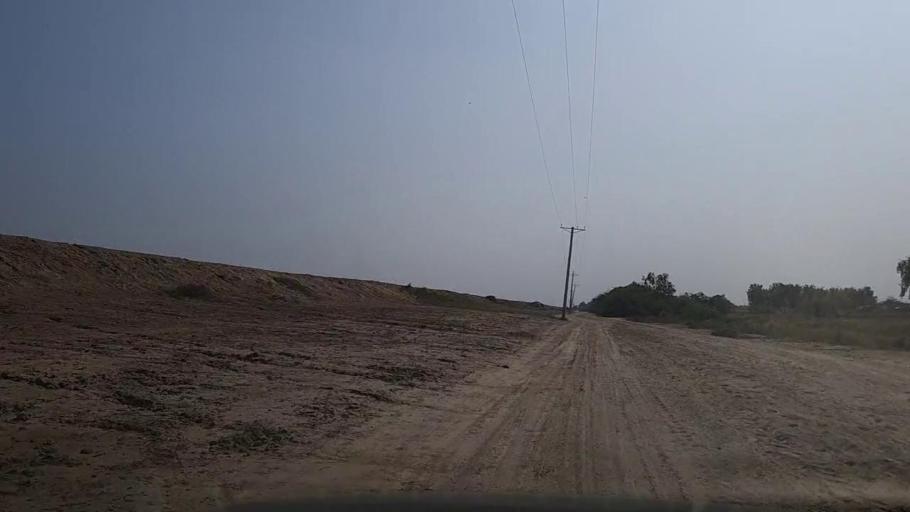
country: PK
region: Sindh
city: Thatta
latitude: 24.5617
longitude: 67.9137
